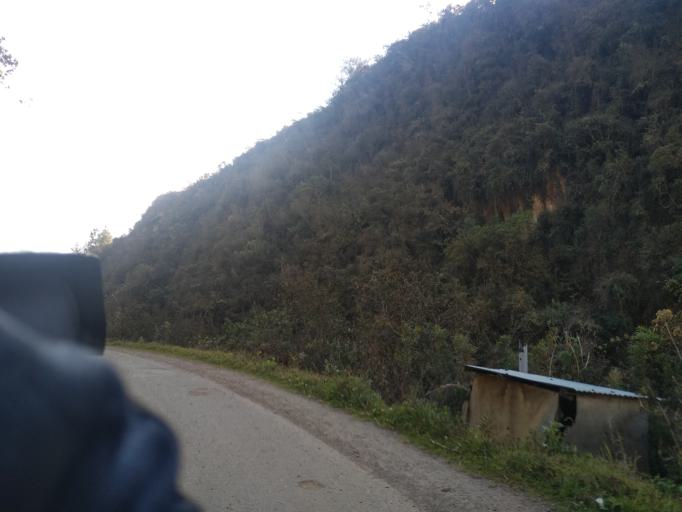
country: PE
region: Amazonas
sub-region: Provincia de Chachapoyas
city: Montevideo
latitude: -6.7255
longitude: -77.8268
